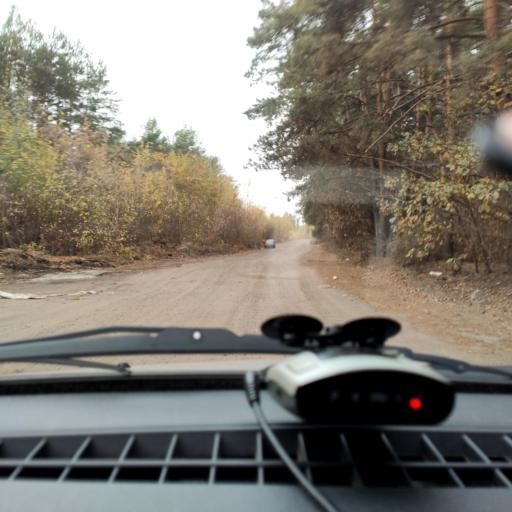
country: RU
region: Voronezj
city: Pridonskoy
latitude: 51.6744
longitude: 39.1246
